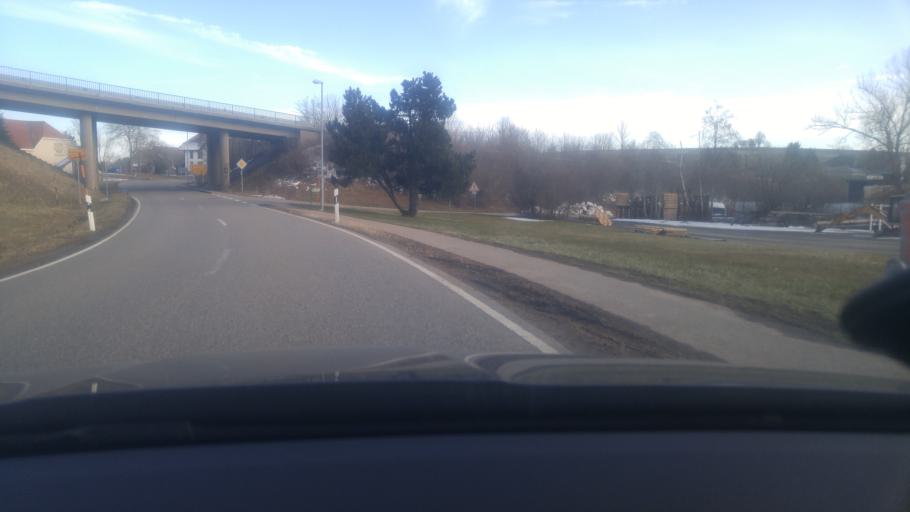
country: DE
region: Baden-Wuerttemberg
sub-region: Freiburg Region
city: Hochenschwand
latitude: 47.6762
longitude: 8.1588
